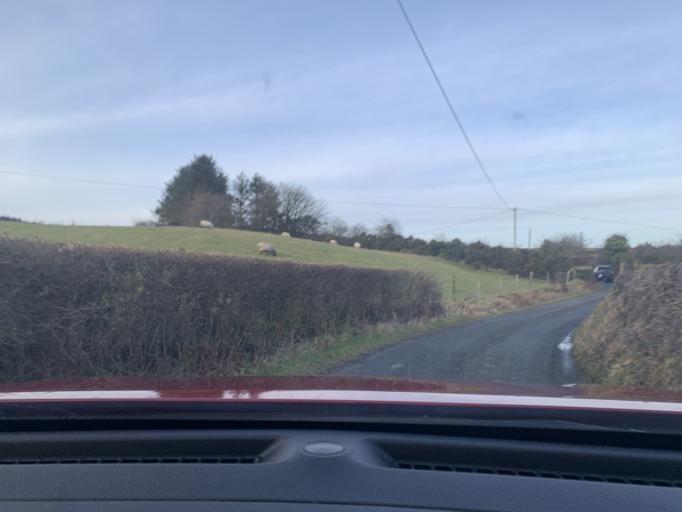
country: IE
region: Connaught
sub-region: Sligo
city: Strandhill
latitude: 54.1750
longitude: -8.6581
